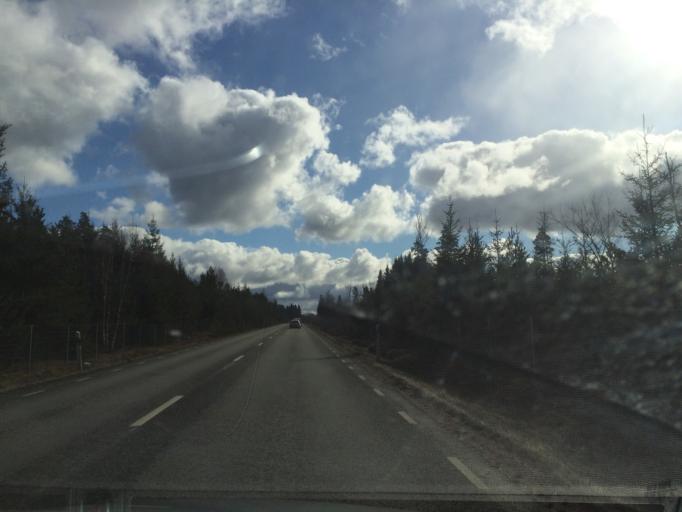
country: SE
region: Vaestra Goetaland
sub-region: Skara Kommun
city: Skara
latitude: 58.3452
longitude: 13.4334
